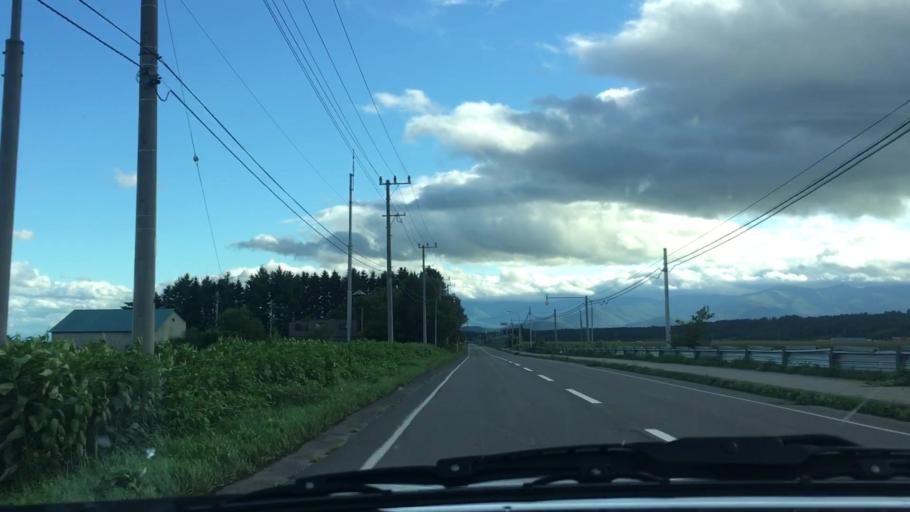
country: JP
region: Hokkaido
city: Otofuke
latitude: 43.1456
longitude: 142.8979
